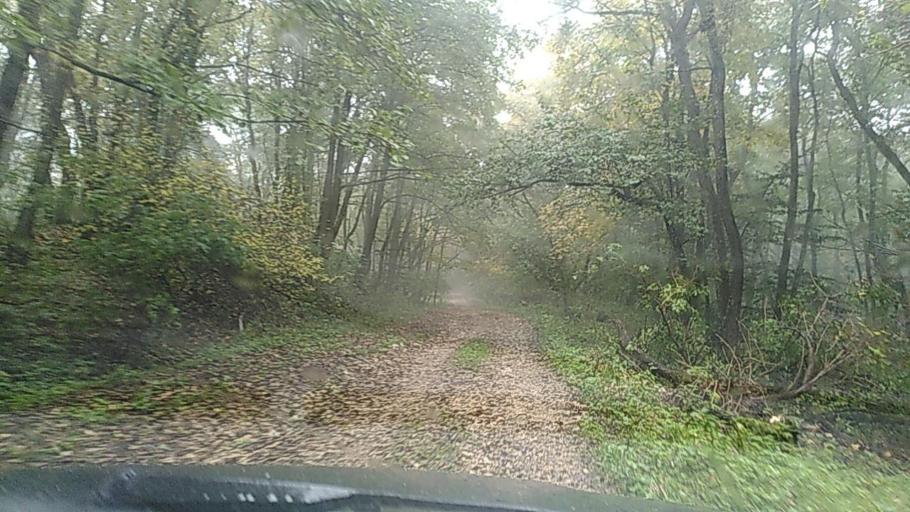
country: RU
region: Kabardino-Balkariya
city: Belaya Rechka
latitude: 43.3582
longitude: 43.4072
